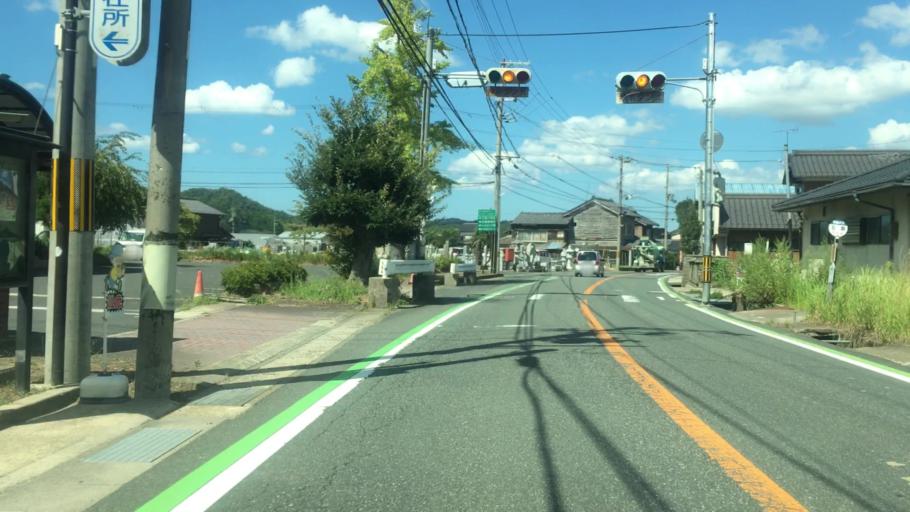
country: JP
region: Kyoto
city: Miyazu
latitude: 35.5895
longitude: 135.0386
